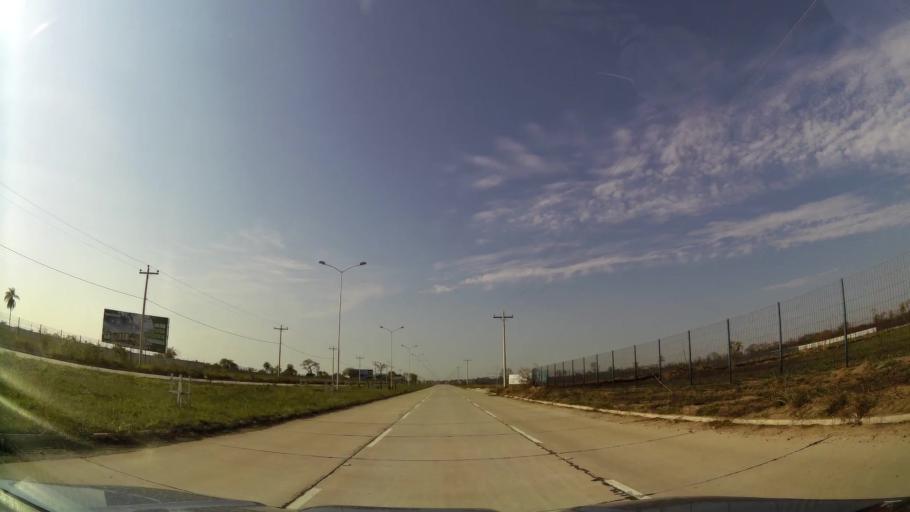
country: BO
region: Santa Cruz
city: Santa Cruz de la Sierra
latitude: -17.6802
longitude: -63.1213
